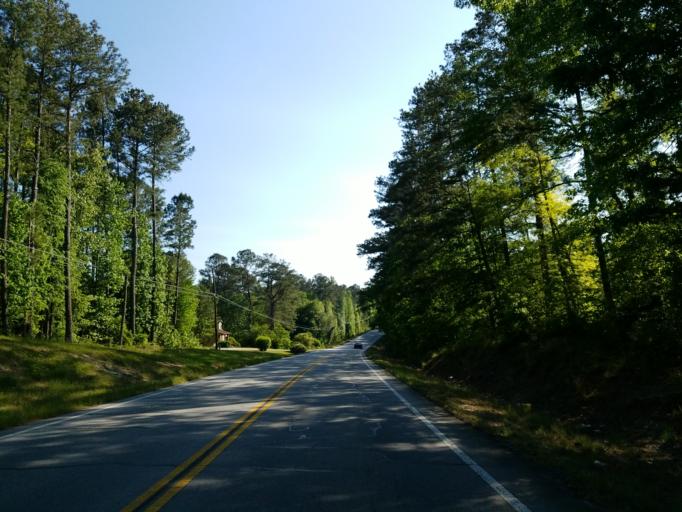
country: US
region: Georgia
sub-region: Paulding County
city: Dallas
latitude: 33.8701
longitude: -84.8871
